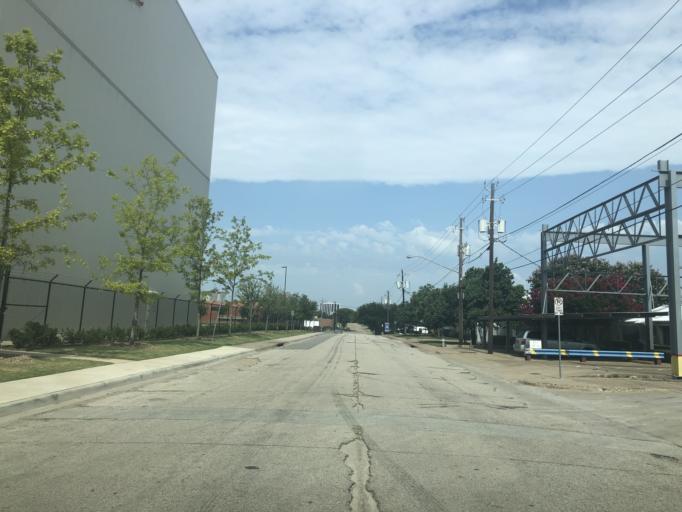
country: US
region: Texas
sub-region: Dallas County
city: Dallas
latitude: 32.8193
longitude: -96.8535
